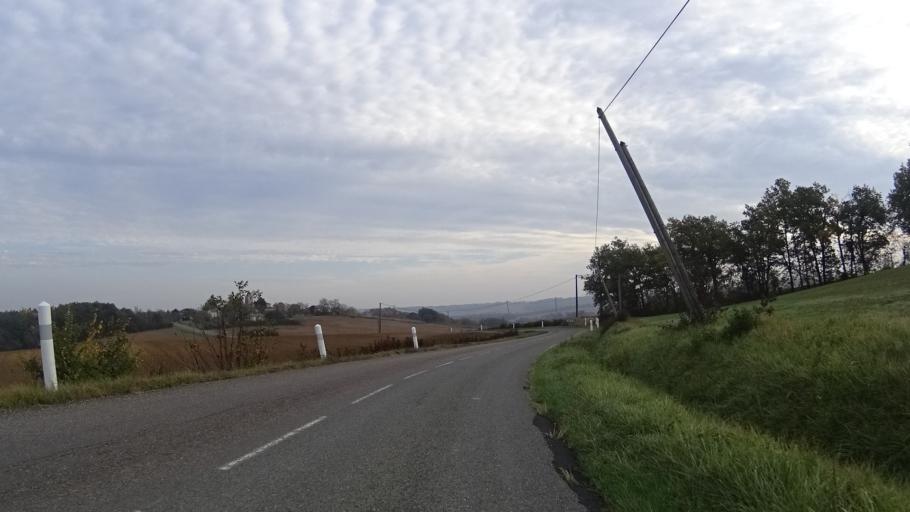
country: FR
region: Aquitaine
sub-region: Departement du Lot-et-Garonne
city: Laplume
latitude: 44.1035
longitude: 0.5681
